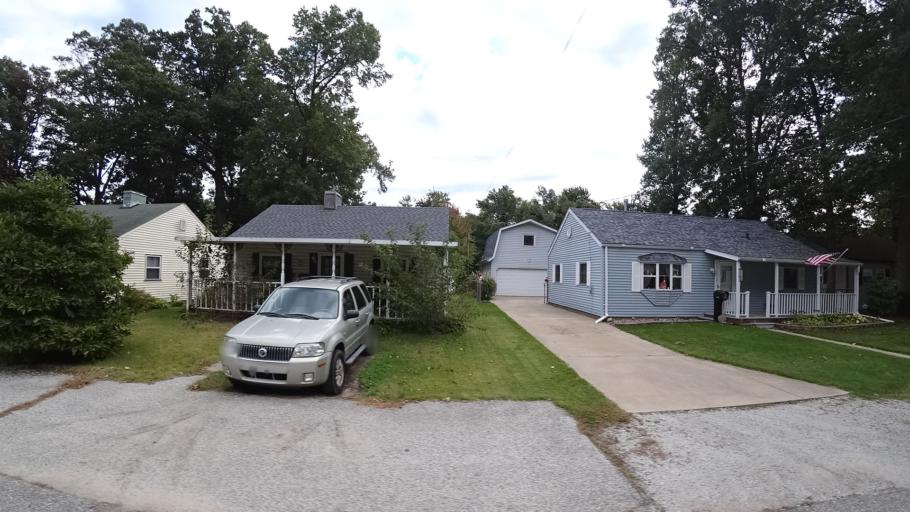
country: US
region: Indiana
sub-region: LaPorte County
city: Michigan City
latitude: 41.6960
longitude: -86.8801
